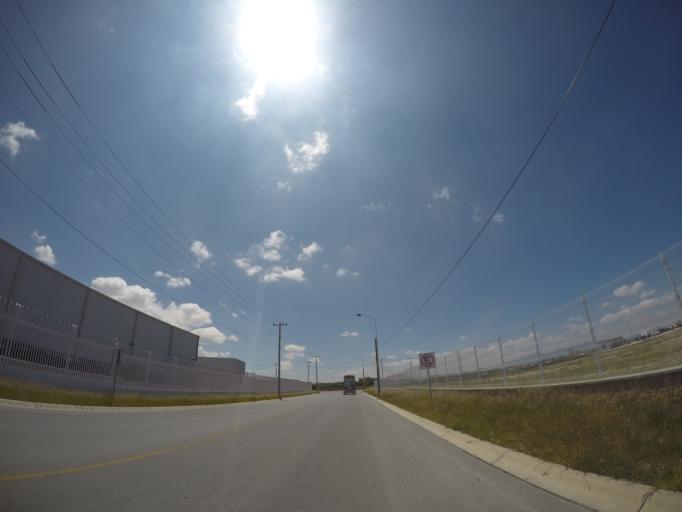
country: MX
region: San Luis Potosi
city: La Pila
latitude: 21.9695
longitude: -100.8738
